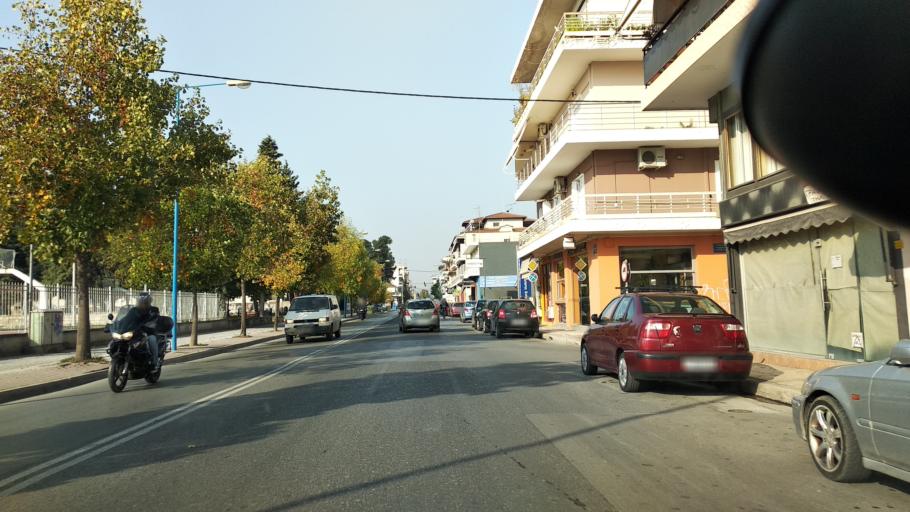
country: GR
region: Thessaly
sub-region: Nomos Larisis
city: Larisa
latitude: 39.6327
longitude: 22.4013
